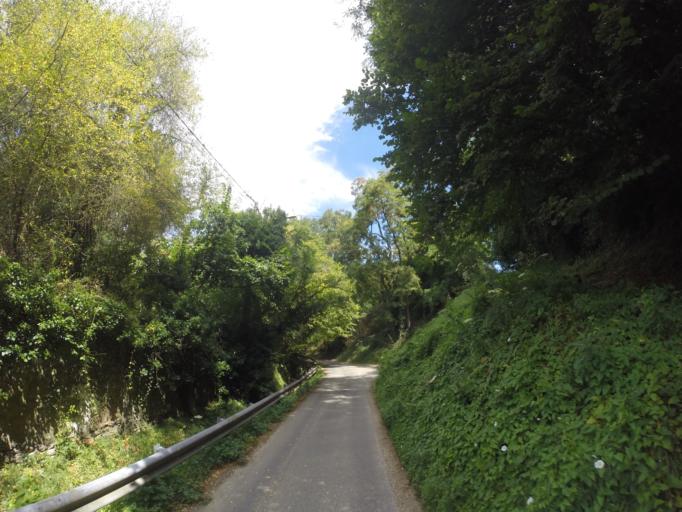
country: FR
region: Centre
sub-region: Departement d'Indre-et-Loire
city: Rochecorbon
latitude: 47.4119
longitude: 0.7168
